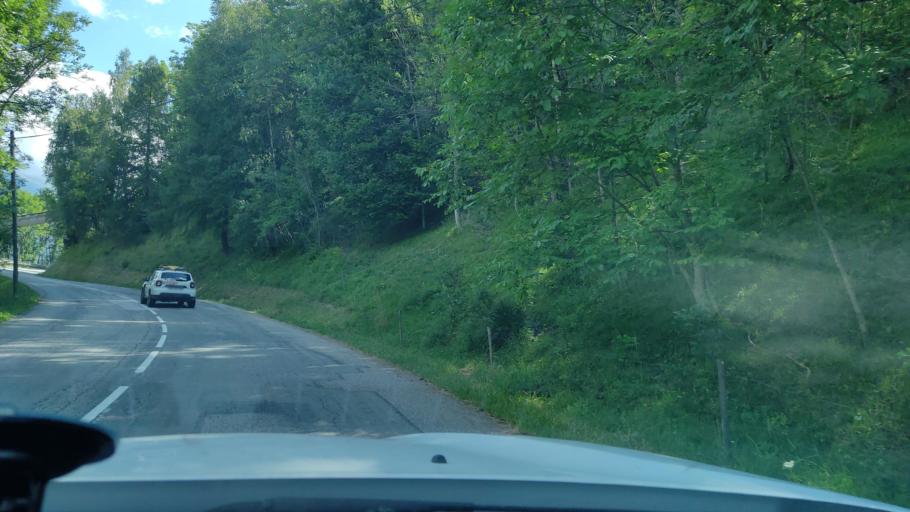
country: FR
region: Rhone-Alpes
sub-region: Departement de la Savoie
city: Bourg-Saint-Maurice
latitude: 45.6041
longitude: 6.7767
